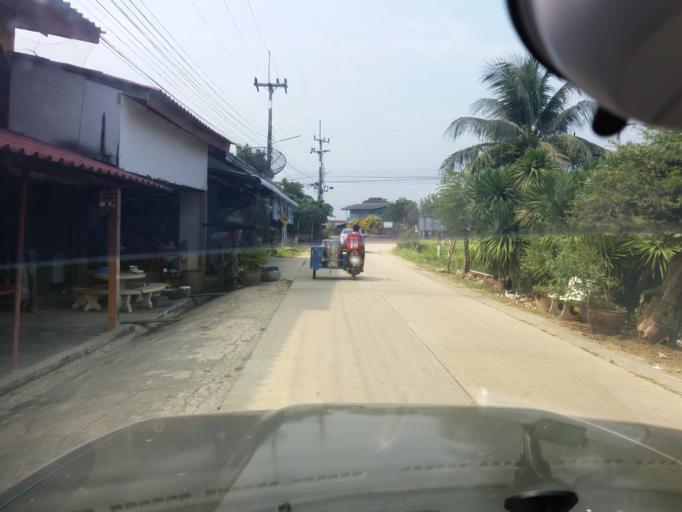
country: TH
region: Suphan Buri
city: Doem Bang Nang Buat
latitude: 14.8920
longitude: 100.1860
